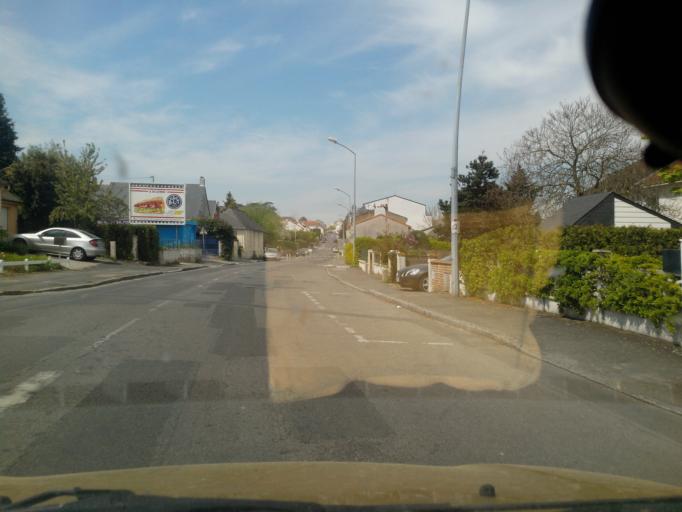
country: FR
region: Pays de la Loire
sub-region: Departement de la Loire-Atlantique
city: Orvault
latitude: 47.2503
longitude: -1.5873
